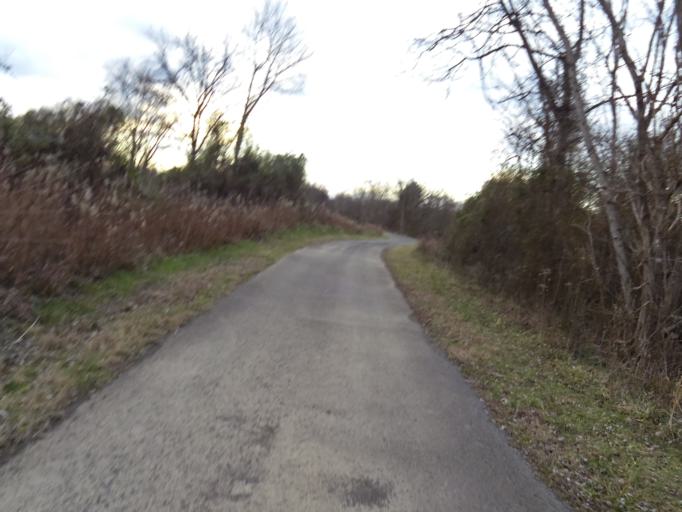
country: US
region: Tennessee
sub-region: Knox County
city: Knoxville
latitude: 35.9577
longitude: -83.8460
